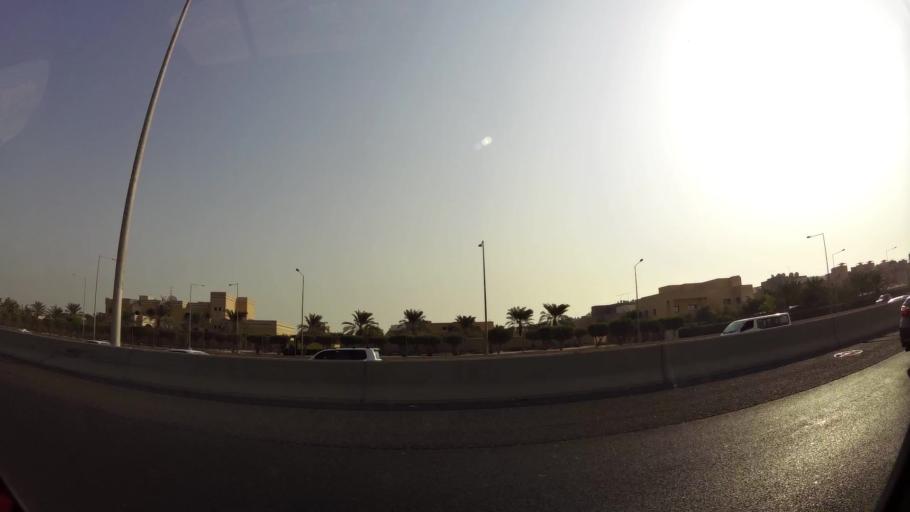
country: KW
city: Al Funaytis
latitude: 29.2396
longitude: 48.0947
